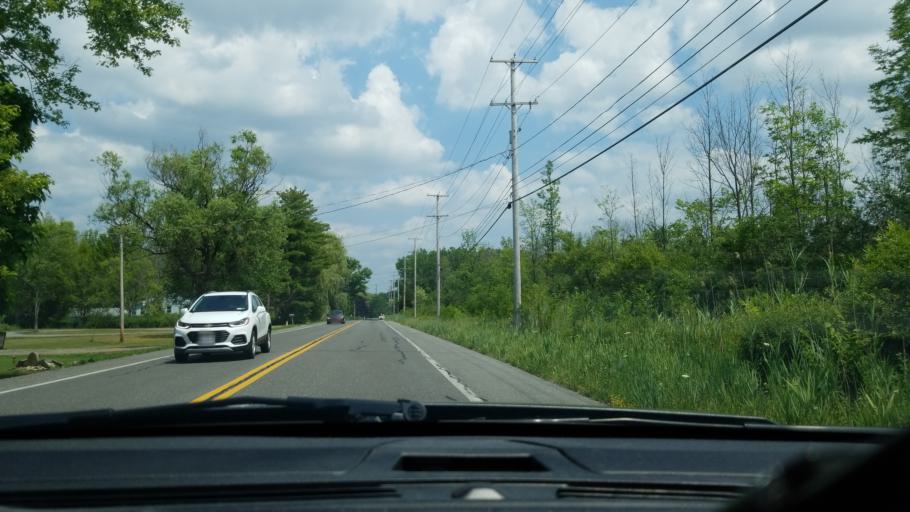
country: US
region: New York
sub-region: Onondaga County
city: Liverpool
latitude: 43.1509
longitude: -76.1995
